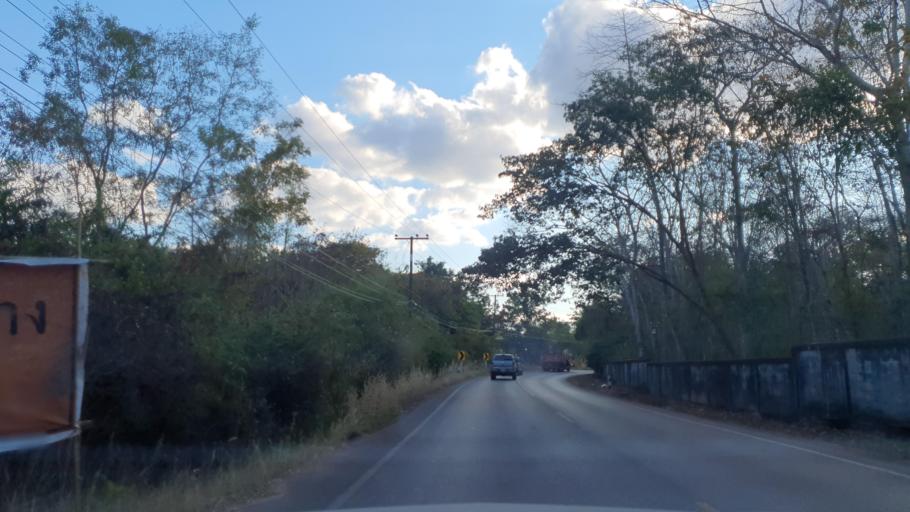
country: TH
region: Changwat Bueng Kan
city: Si Wilai
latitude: 18.1317
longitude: 103.8846
